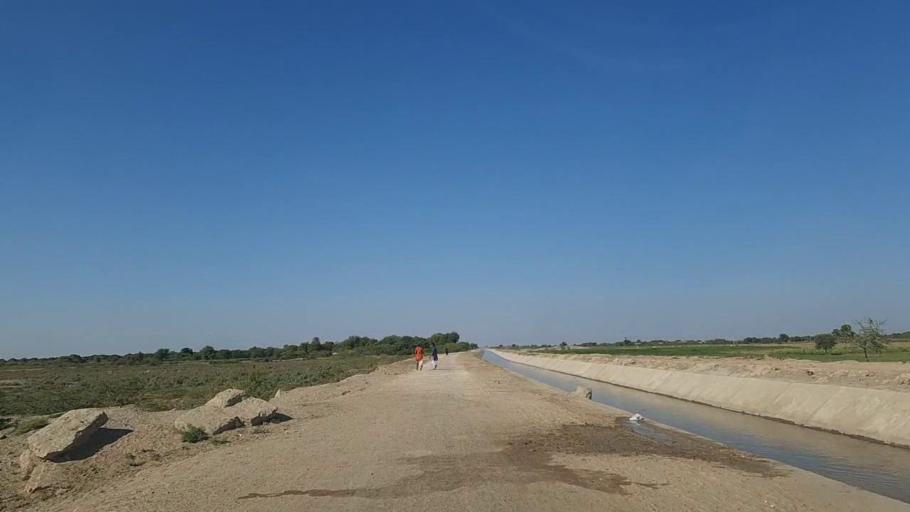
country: PK
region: Sindh
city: Kunri
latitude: 25.2269
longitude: 69.5149
